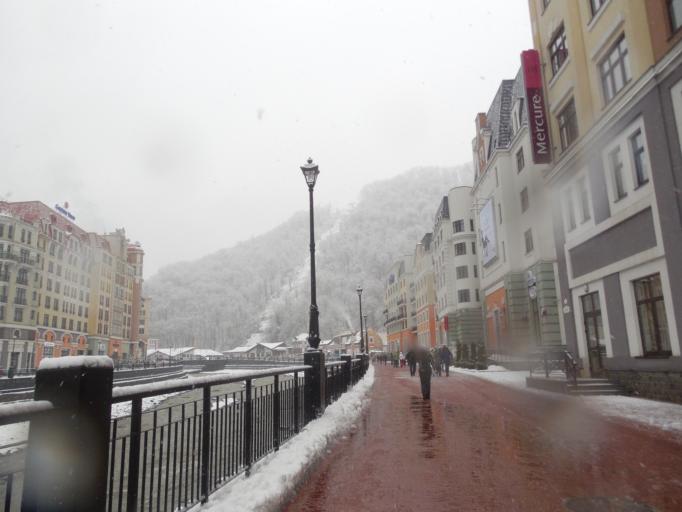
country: RU
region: Krasnodarskiy
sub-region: Sochi City
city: Krasnaya Polyana
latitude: 43.6721
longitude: 40.2933
